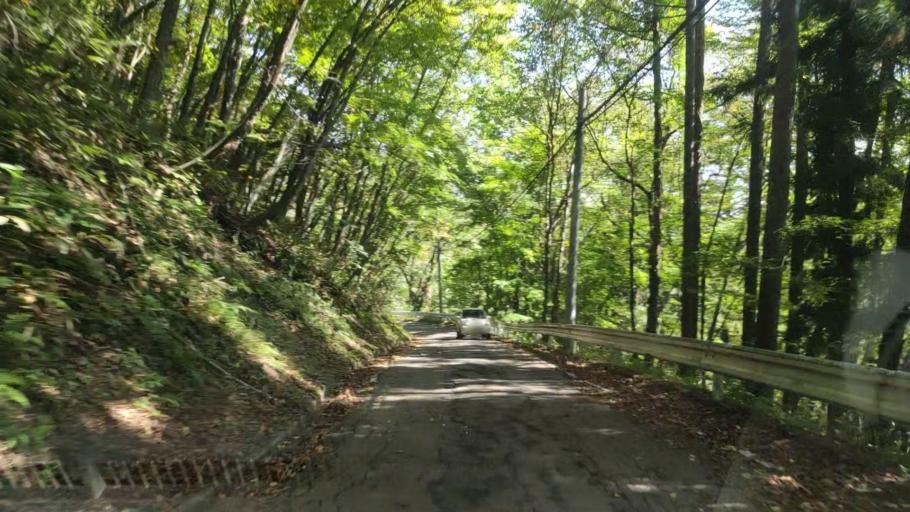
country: JP
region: Gunma
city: Nakanojomachi
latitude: 36.6592
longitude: 138.6264
